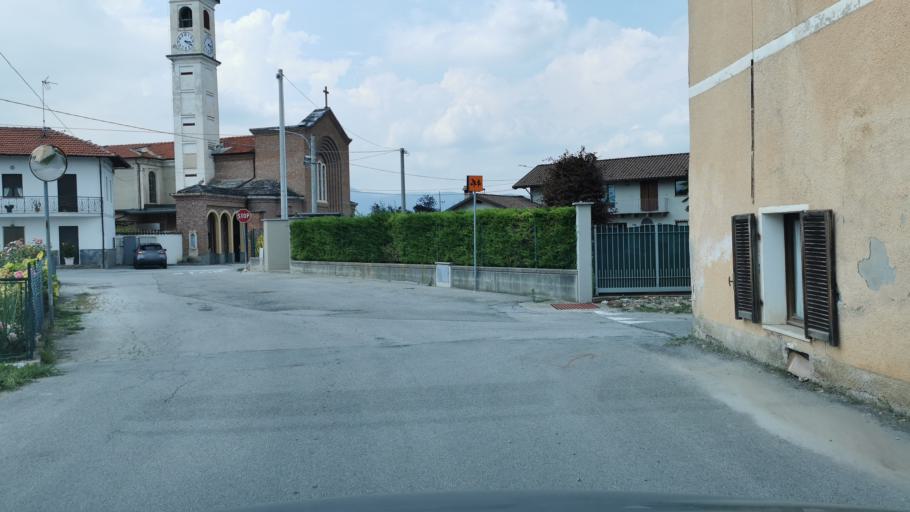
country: IT
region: Piedmont
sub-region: Provincia di Cuneo
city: Caraglio
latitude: 44.4304
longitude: 7.4503
